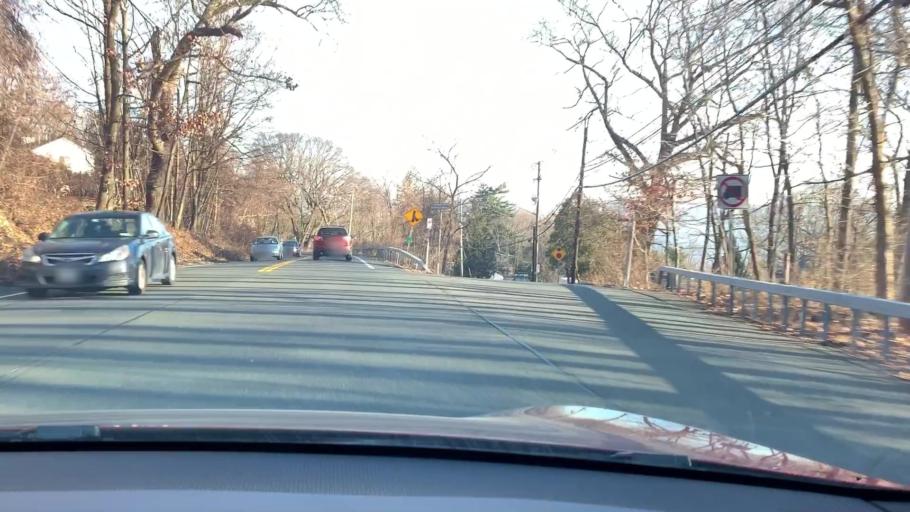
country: US
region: New York
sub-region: Rockland County
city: Piermont
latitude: 41.0400
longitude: -73.9214
